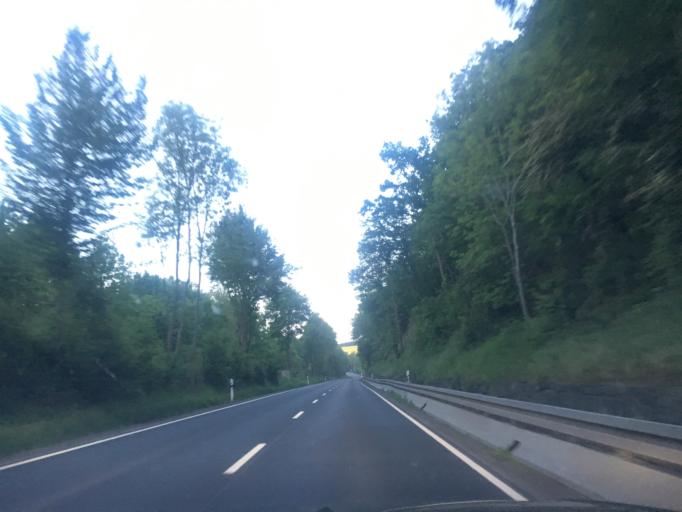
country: DE
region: Thuringia
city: Gera
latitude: 50.8392
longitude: 12.0752
